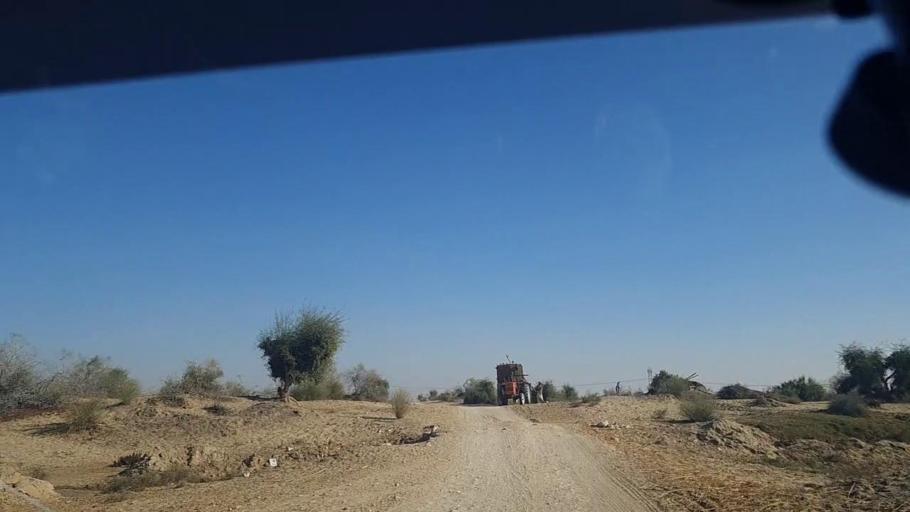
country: PK
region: Sindh
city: Khanpur
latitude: 27.6475
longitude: 69.3950
